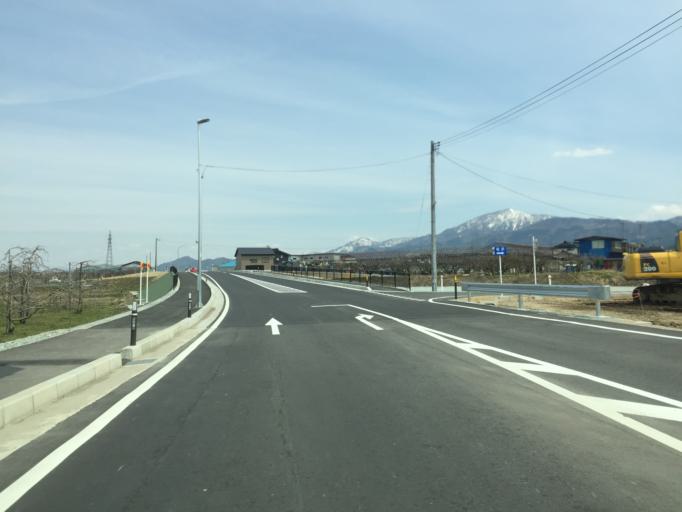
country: JP
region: Yamagata
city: Higashine
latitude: 38.4479
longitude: 140.3550
